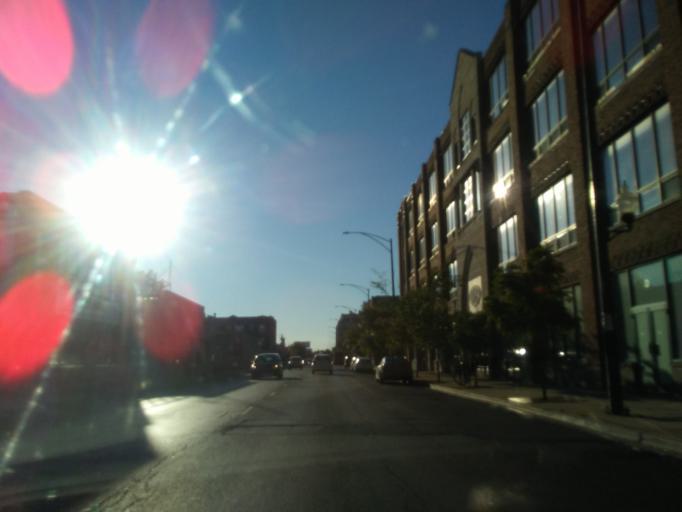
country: US
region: Illinois
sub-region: Cook County
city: Lincolnwood
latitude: 41.9390
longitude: -87.7311
